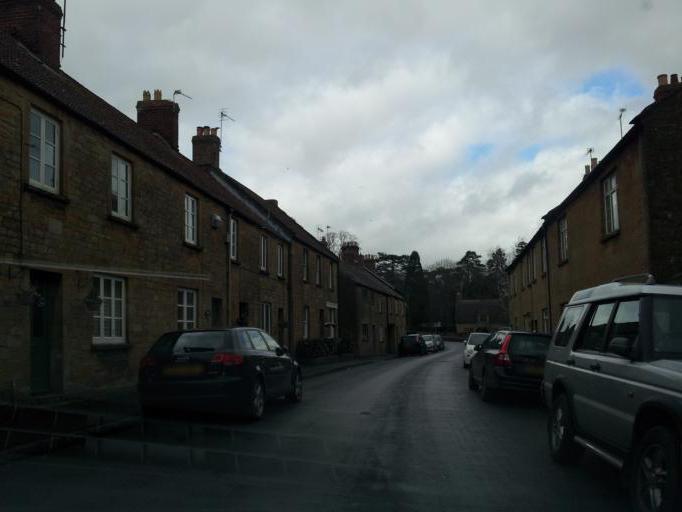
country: GB
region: England
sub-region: Somerset
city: Stoke-sub-Hamdon
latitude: 50.9507
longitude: -2.7182
